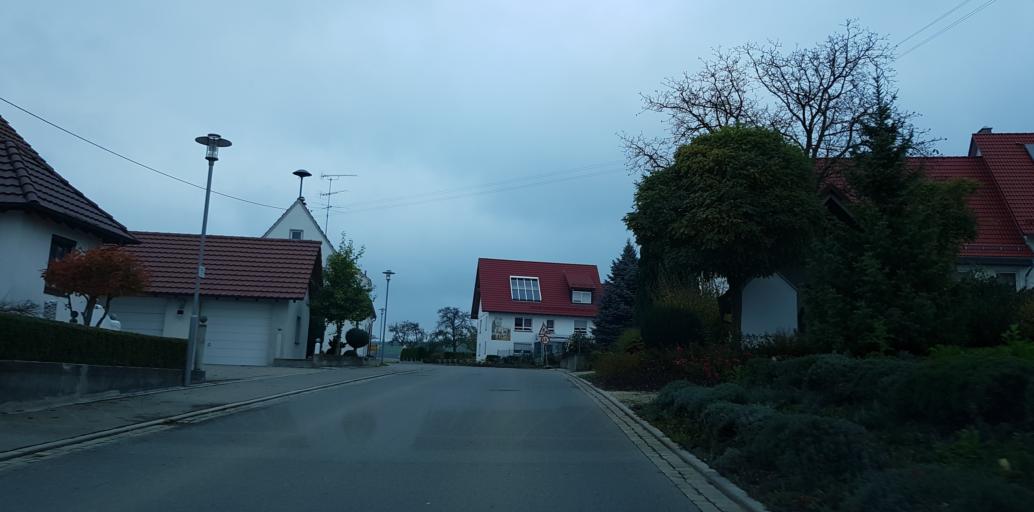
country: DE
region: Baden-Wuerttemberg
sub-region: Tuebingen Region
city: Altheim
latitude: 48.3108
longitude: 9.7866
